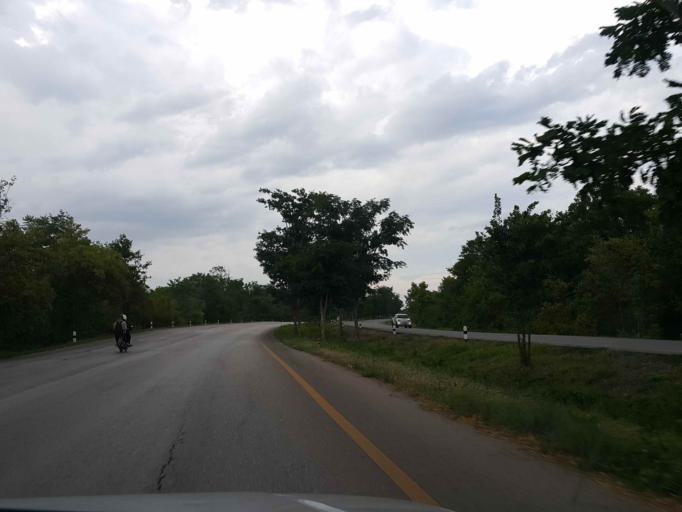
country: TH
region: Lampang
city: Sop Prap
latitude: 17.9793
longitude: 99.3556
